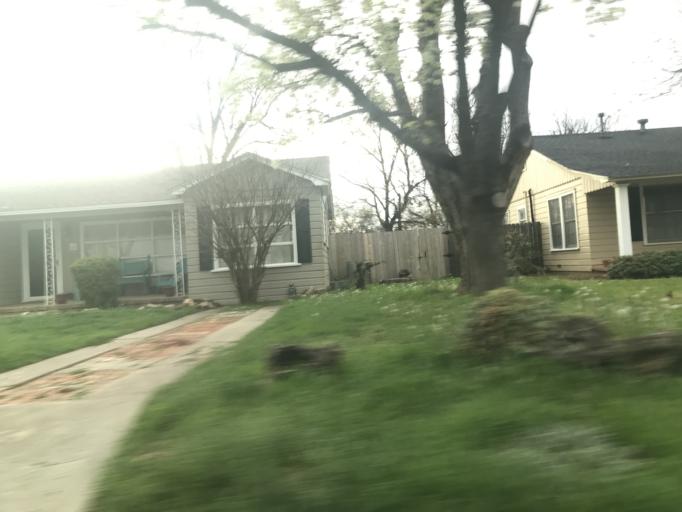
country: US
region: Texas
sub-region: Taylor County
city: Abilene
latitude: 32.4412
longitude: -99.7657
